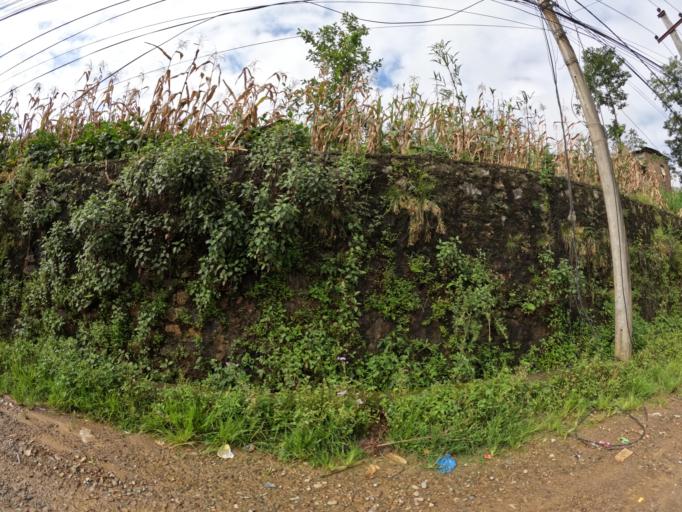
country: NP
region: Central Region
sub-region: Bagmati Zone
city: Kathmandu
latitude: 27.7669
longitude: 85.3322
